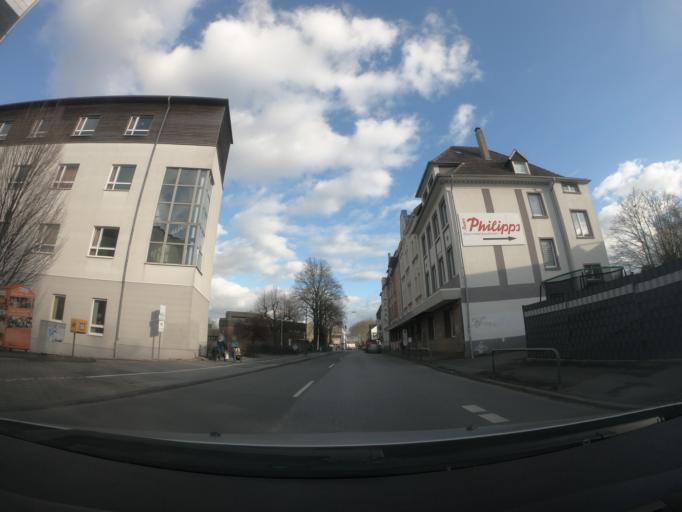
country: DE
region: North Rhine-Westphalia
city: Lunen
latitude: 51.5695
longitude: 7.5187
